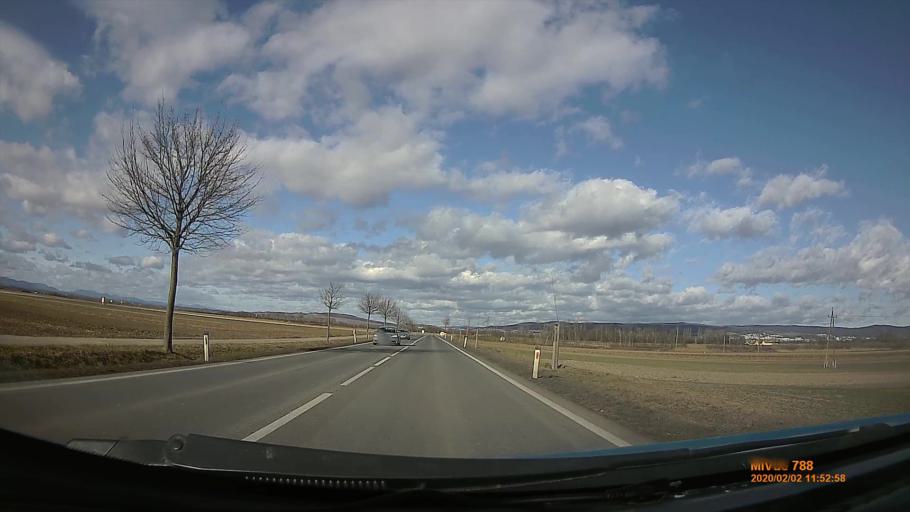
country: AT
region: Burgenland
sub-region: Eisenstadt-Umgebung
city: Zagersdorf
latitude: 47.7794
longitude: 16.5236
